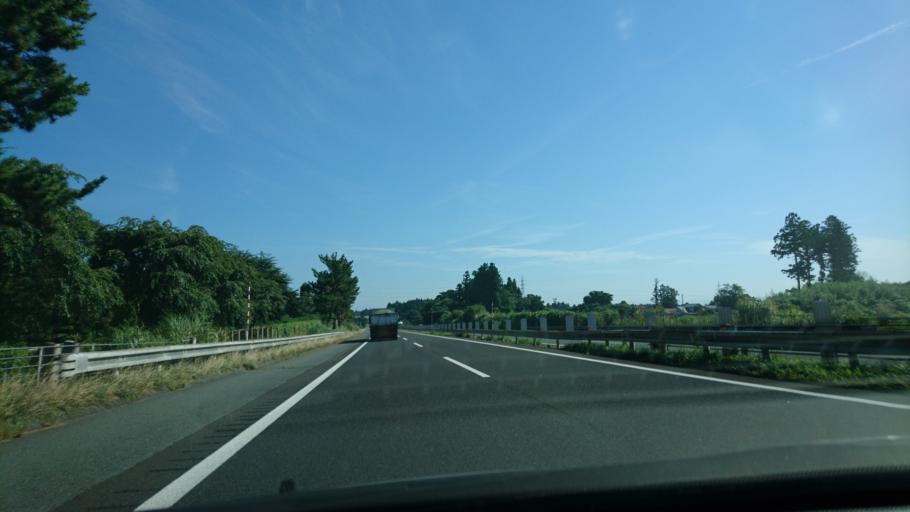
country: JP
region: Iwate
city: Mizusawa
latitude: 39.0906
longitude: 141.1095
